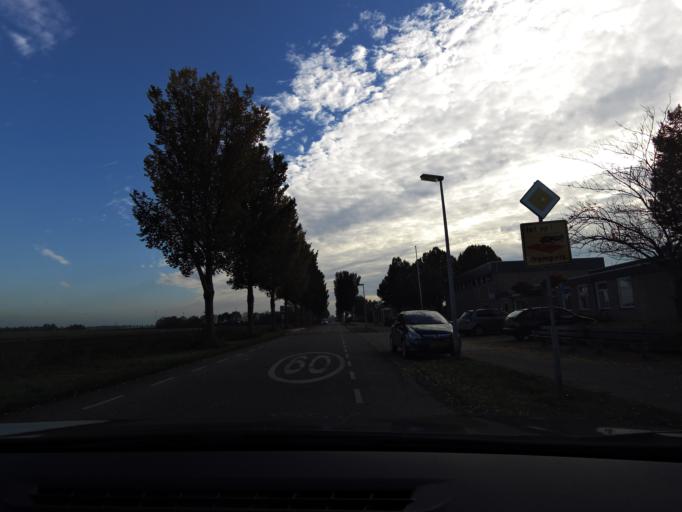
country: NL
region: North Brabant
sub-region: Gemeente Steenbergen
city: Dinteloord
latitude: 51.7146
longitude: 4.2894
